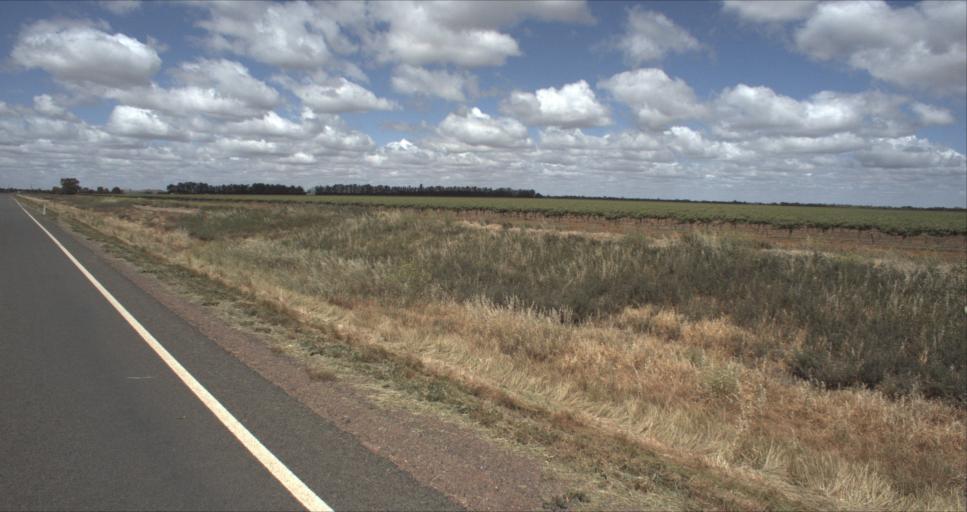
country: AU
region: New South Wales
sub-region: Murrumbidgee Shire
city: Darlington Point
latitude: -34.4895
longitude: 146.1632
